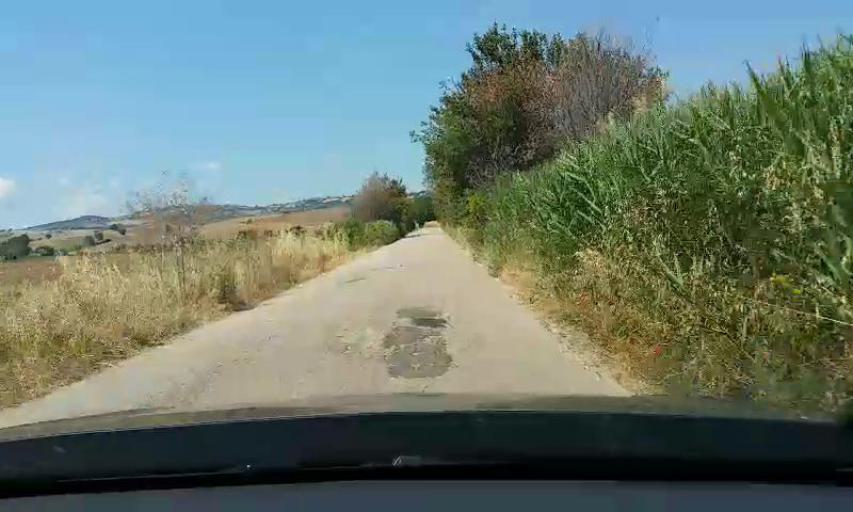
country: IT
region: Molise
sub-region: Provincia di Campobasso
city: Montecilfone
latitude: 41.9304
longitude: 14.8594
